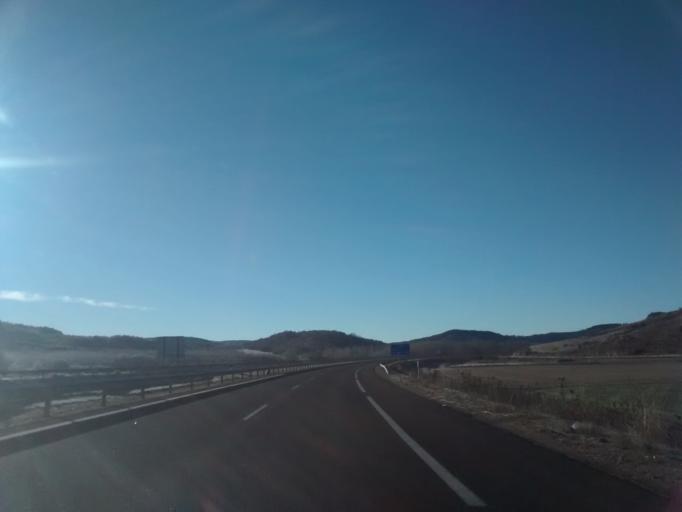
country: ES
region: Castille and Leon
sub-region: Provincia de Palencia
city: Alar del Rey
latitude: 42.7105
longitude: -4.2883
